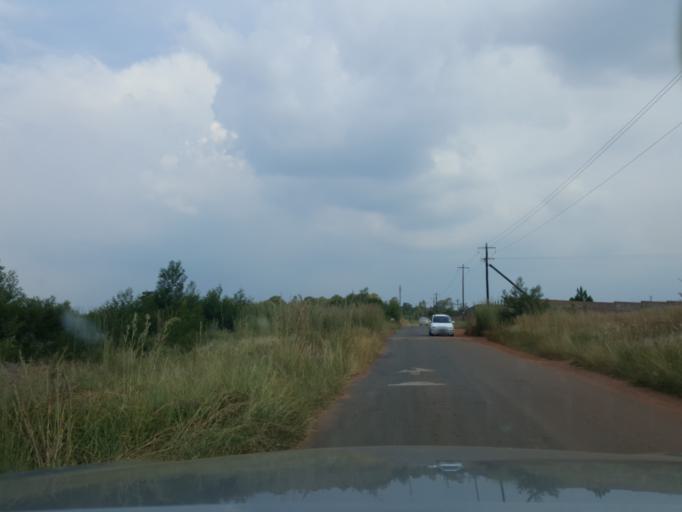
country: ZA
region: Gauteng
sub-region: City of Tshwane Metropolitan Municipality
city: Centurion
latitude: -25.8601
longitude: 28.3272
